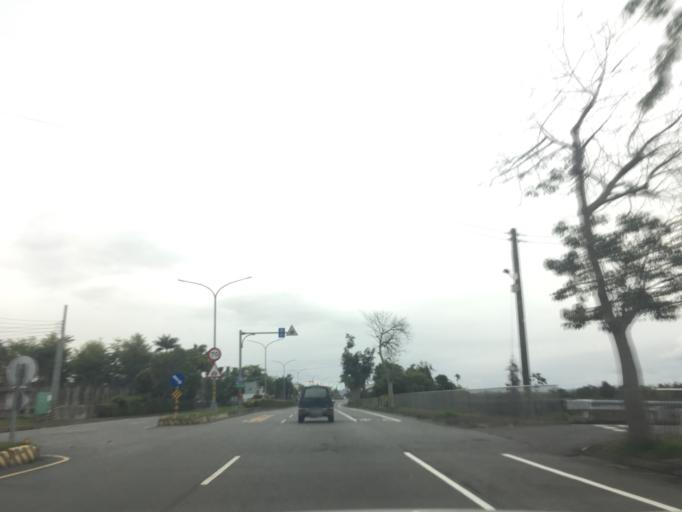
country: TW
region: Taiwan
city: Taitung City
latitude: 22.7142
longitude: 121.0473
